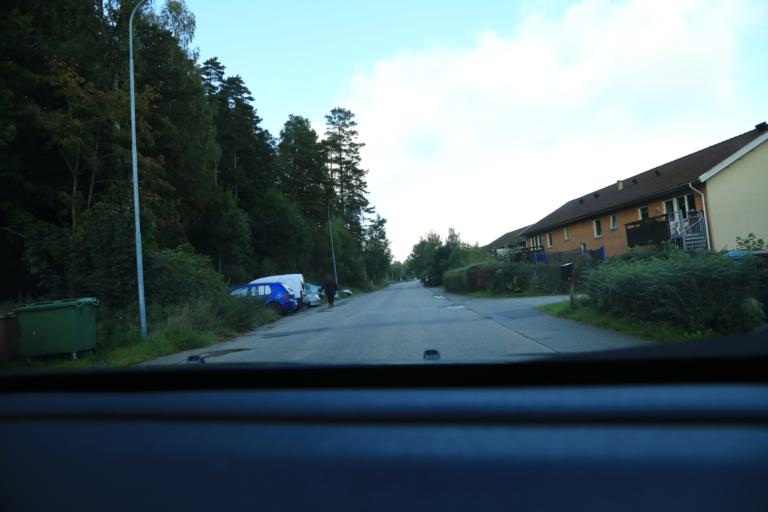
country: SE
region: Halland
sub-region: Halmstads Kommun
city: Getinge
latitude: 57.1391
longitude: 12.7181
